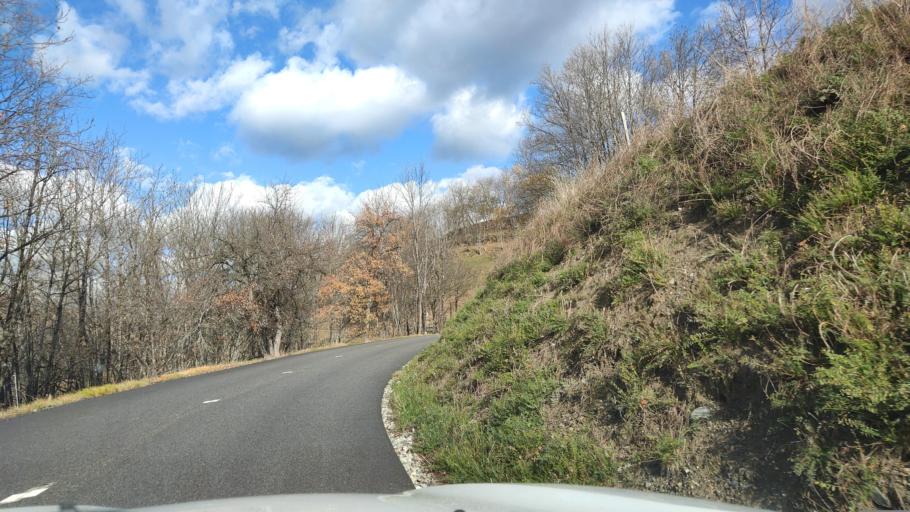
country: FR
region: Rhone-Alpes
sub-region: Departement de la Savoie
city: Saint-Jean-de-Maurienne
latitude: 45.2195
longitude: 6.3203
